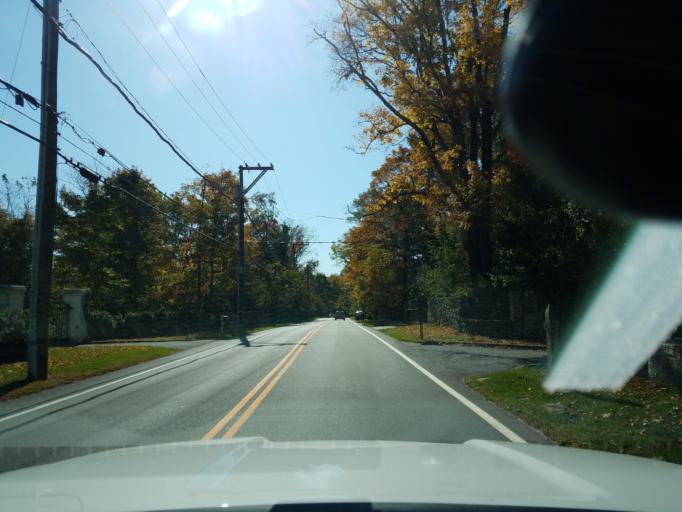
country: US
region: Connecticut
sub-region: Fairfield County
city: Glenville
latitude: 41.0917
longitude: -73.6318
